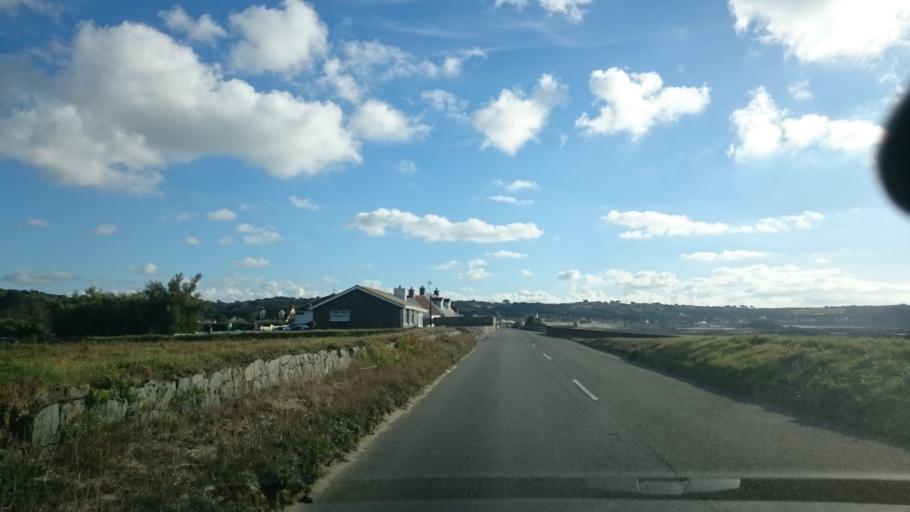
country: GG
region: St Peter Port
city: Saint Peter Port
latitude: 49.4519
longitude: -2.6500
